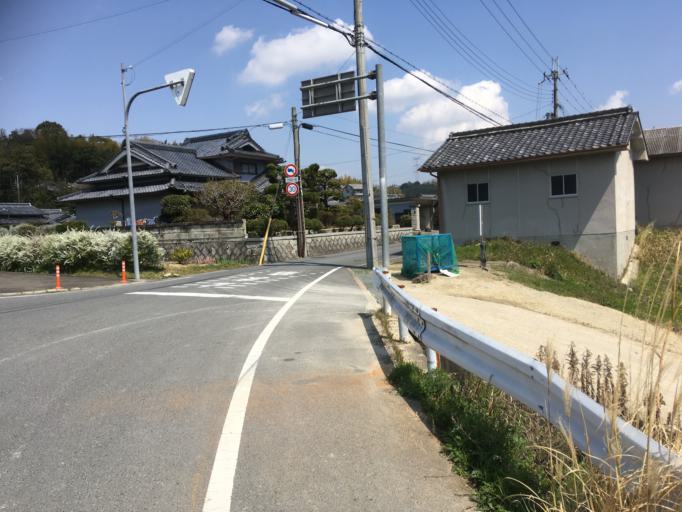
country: JP
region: Nara
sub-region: Ikoma-shi
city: Ikoma
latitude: 34.7515
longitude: 135.7187
